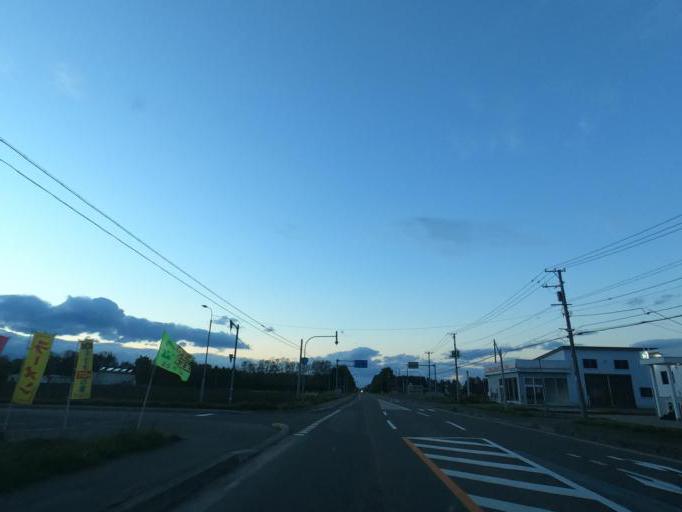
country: JP
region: Hokkaido
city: Obihiro
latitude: 42.6541
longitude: 143.1889
